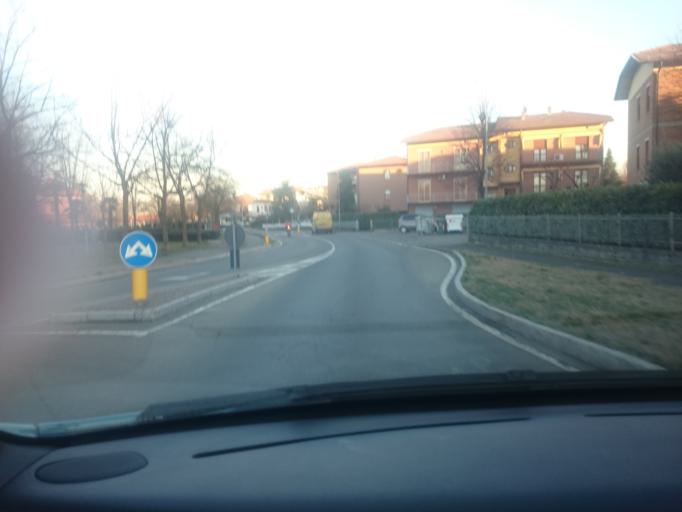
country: IT
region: Emilia-Romagna
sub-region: Provincia di Reggio Emilia
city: Scandiano
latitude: 44.5924
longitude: 10.6954
